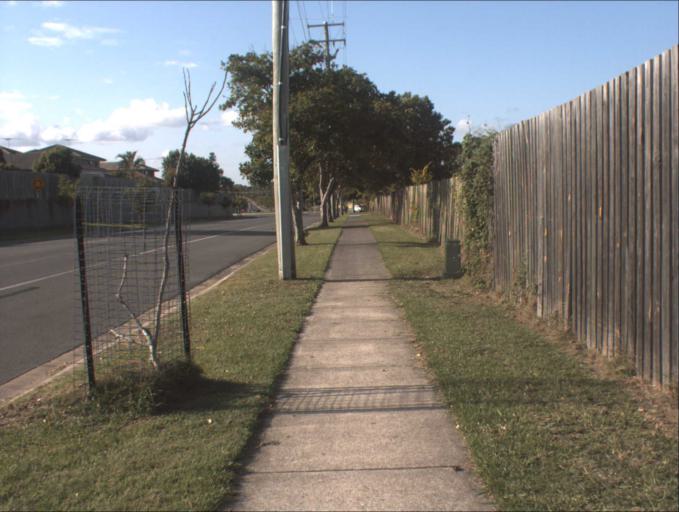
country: AU
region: Queensland
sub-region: Logan
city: Park Ridge South
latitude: -27.6832
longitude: 153.0506
